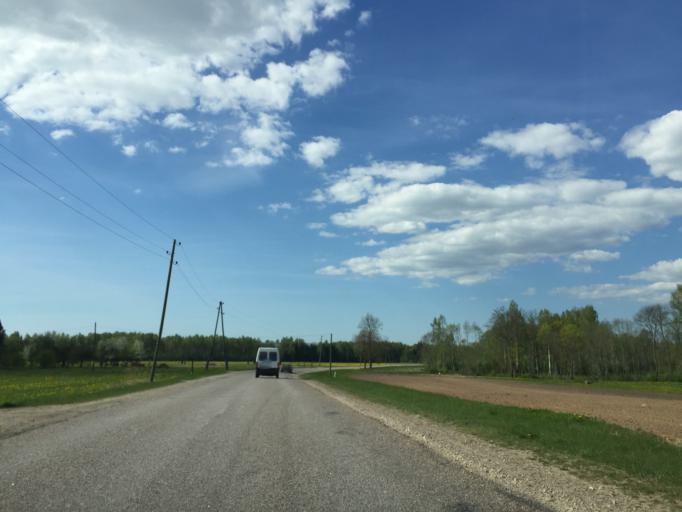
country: LV
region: Limbazu Rajons
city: Limbazi
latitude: 57.4642
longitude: 24.7153
